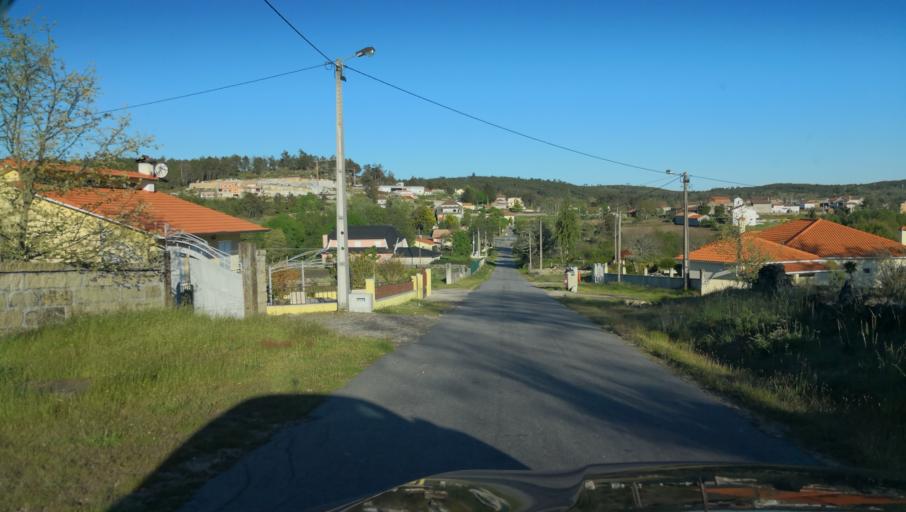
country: PT
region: Vila Real
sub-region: Vila Real
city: Vila Real
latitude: 41.3557
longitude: -7.6492
